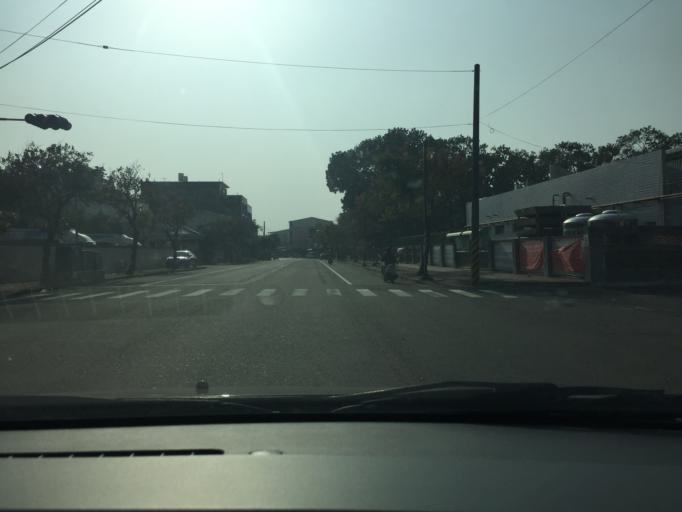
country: TW
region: Taiwan
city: Xinying
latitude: 23.1872
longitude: 120.2636
